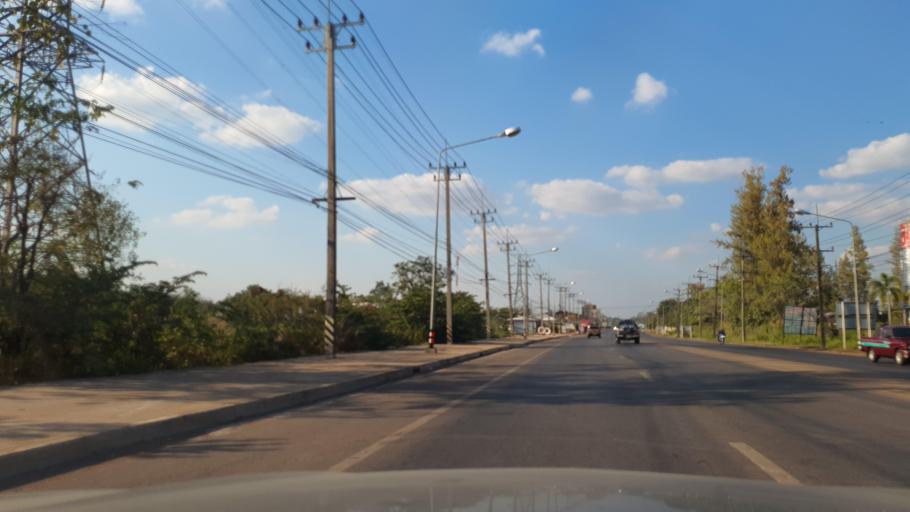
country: TH
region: Sakon Nakhon
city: Sakon Nakhon
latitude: 17.1465
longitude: 104.1084
